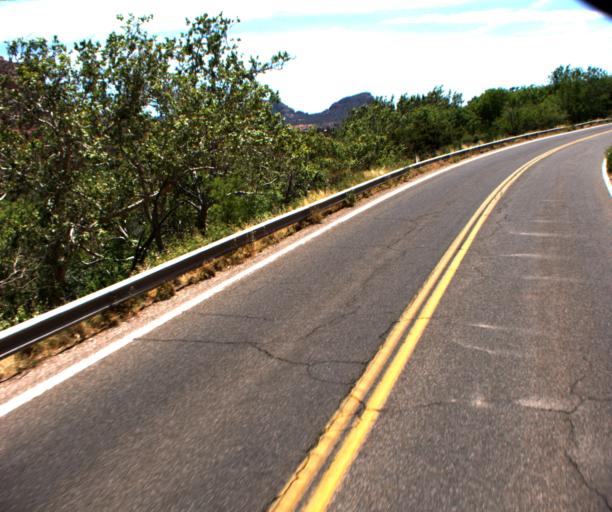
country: US
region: Arizona
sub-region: Coconino County
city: Sedona
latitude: 34.8742
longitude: -111.7556
